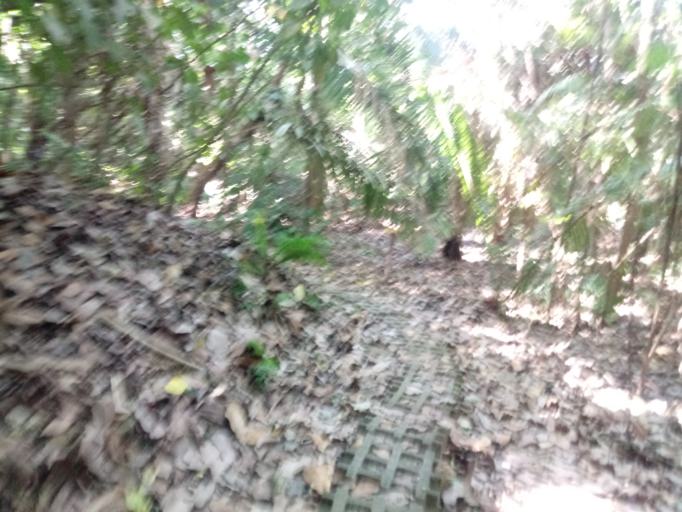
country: CR
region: Puntarenas
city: Paquera
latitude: 9.5857
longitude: -85.0990
